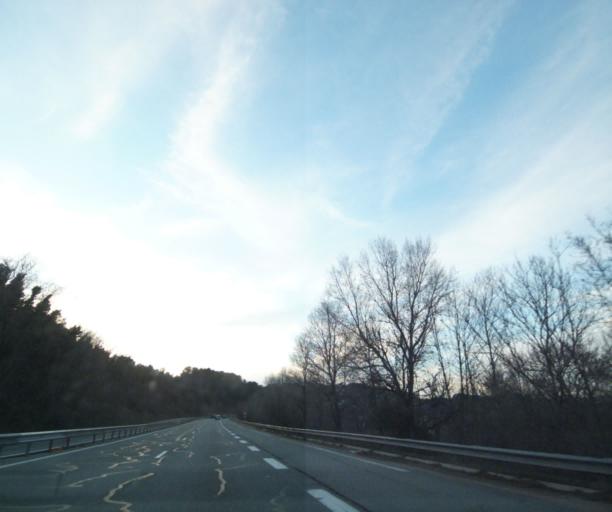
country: FR
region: Provence-Alpes-Cote d'Azur
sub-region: Departement du Var
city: Trans-en-Provence
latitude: 43.4936
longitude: 6.5005
